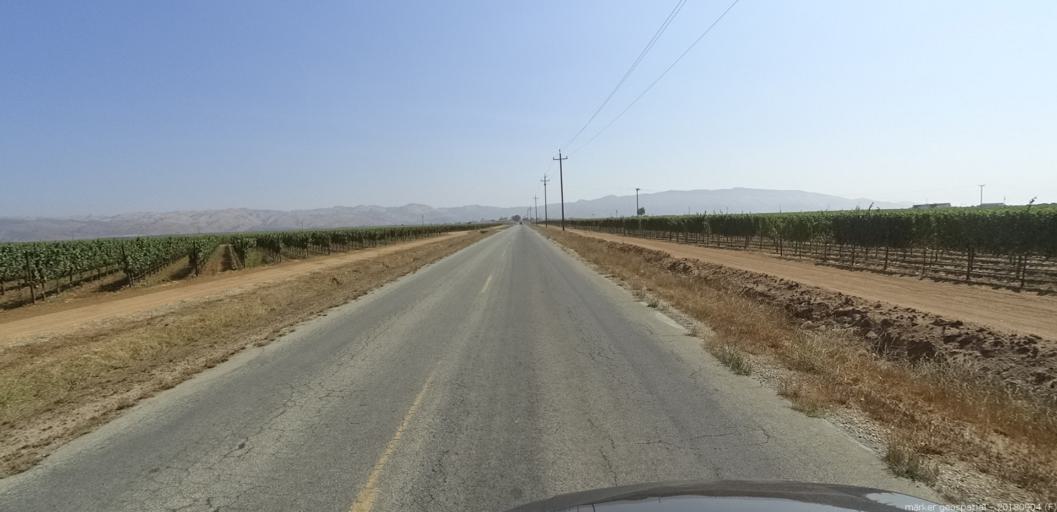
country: US
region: California
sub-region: Monterey County
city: Gonzales
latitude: 36.5003
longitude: -121.4008
